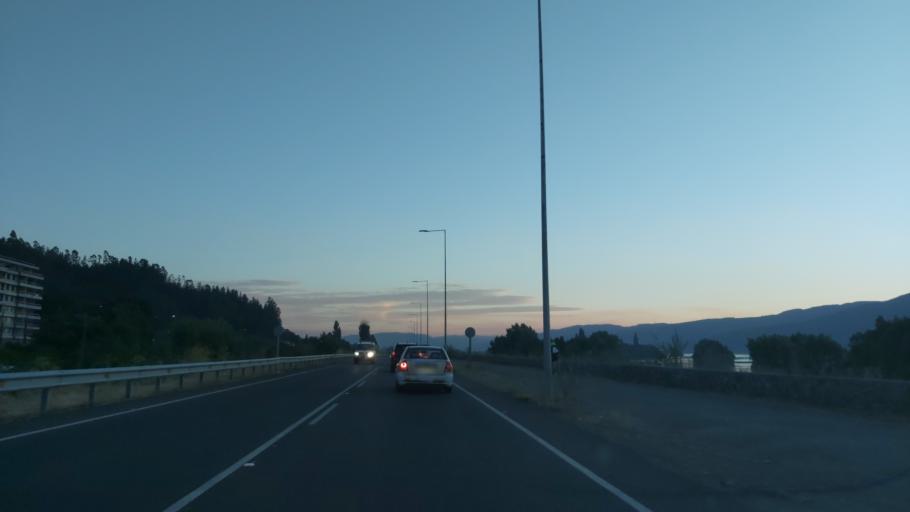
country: CL
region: Biobio
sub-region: Provincia de Concepcion
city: Chiguayante
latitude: -36.8811
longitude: -73.0388
